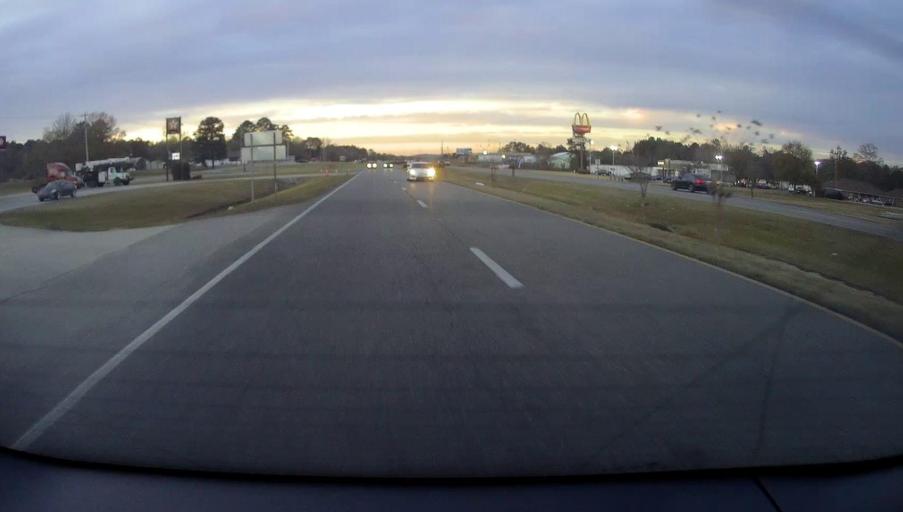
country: US
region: Alabama
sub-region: Etowah County
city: Glencoe
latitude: 33.9659
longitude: -85.9429
